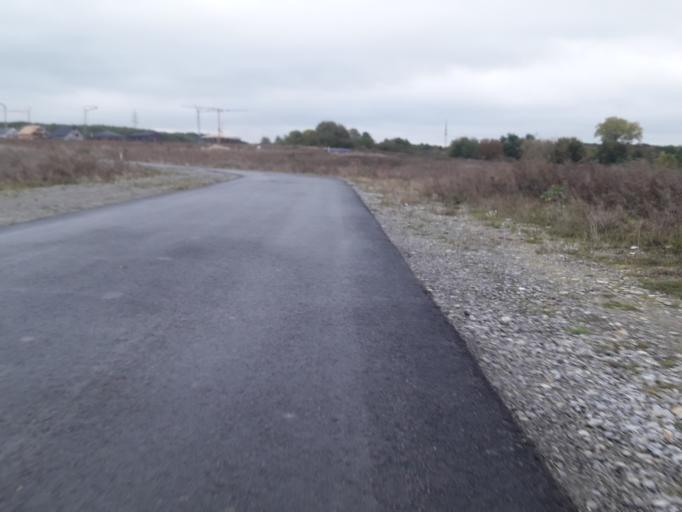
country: DE
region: North Rhine-Westphalia
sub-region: Regierungsbezirk Detmold
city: Paderborn
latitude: 51.7175
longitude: 8.8029
